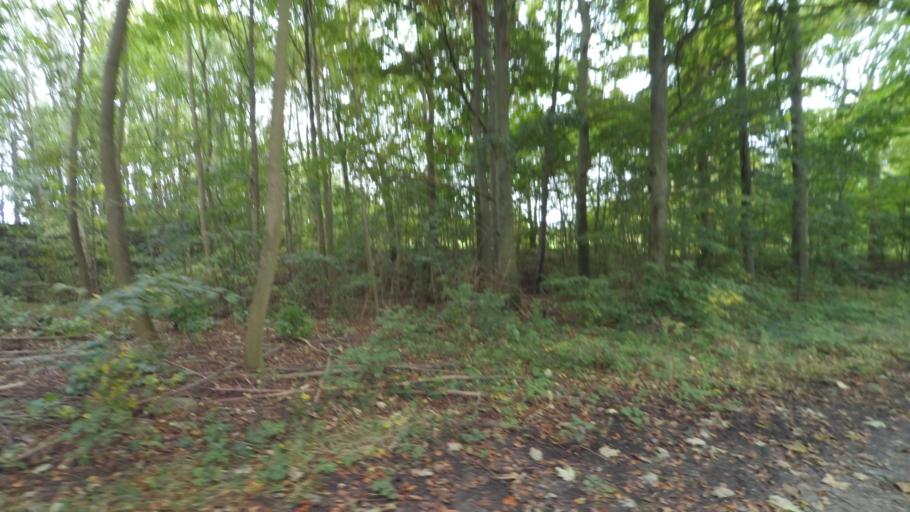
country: DK
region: Central Jutland
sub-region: Arhus Kommune
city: Kolt
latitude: 56.1390
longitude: 10.0837
